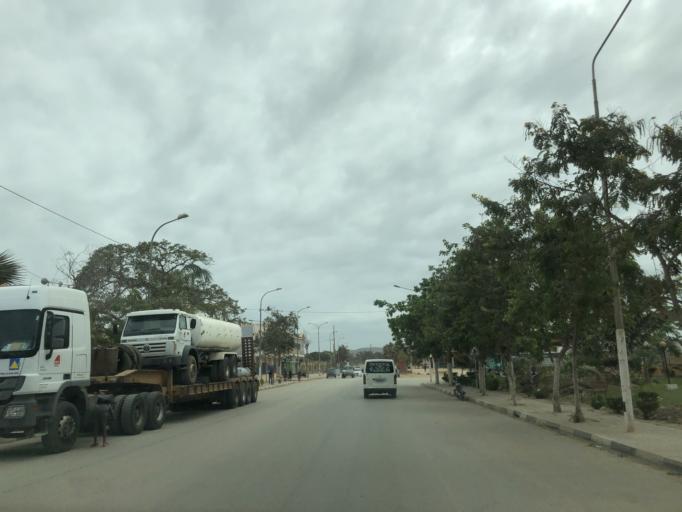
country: AO
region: Cuanza Sul
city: Sumbe
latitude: -11.2013
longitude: 13.8445
